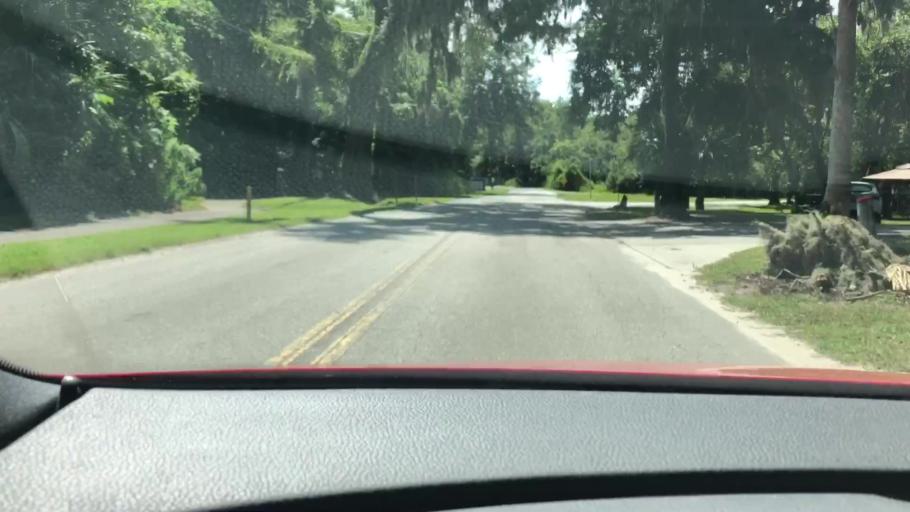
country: US
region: Florida
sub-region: Volusia County
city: New Smyrna Beach
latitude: 29.0180
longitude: -80.9281
